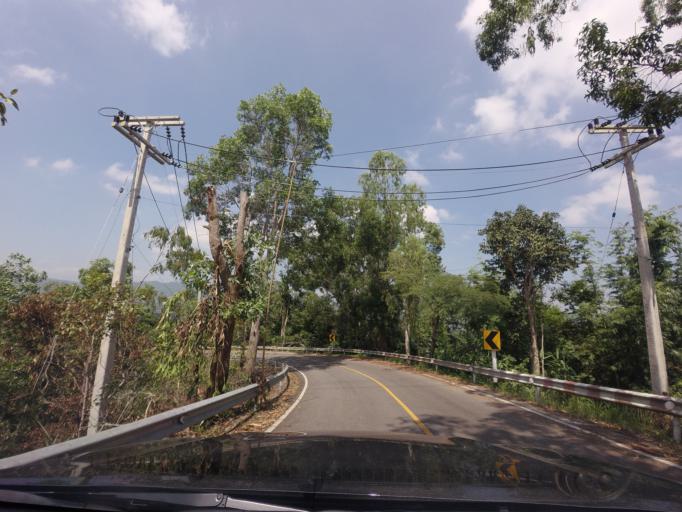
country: TH
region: Loei
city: Na Haeo
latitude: 17.4947
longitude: 100.8972
